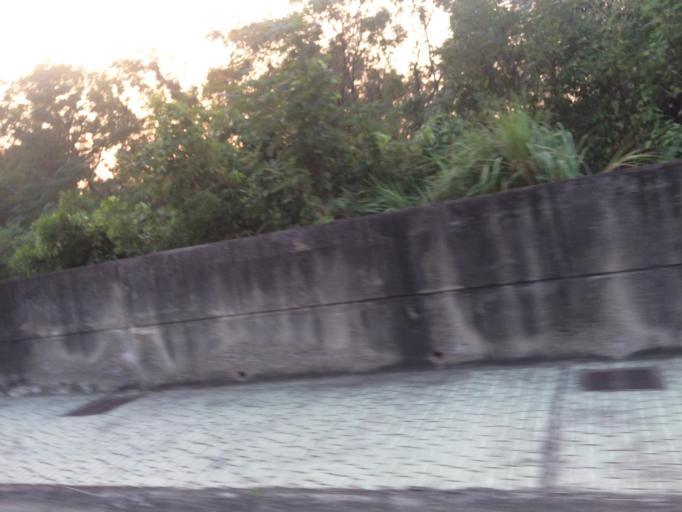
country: TW
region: Taiwan
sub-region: Hsinchu
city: Hsinchu
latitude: 24.7054
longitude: 120.9258
